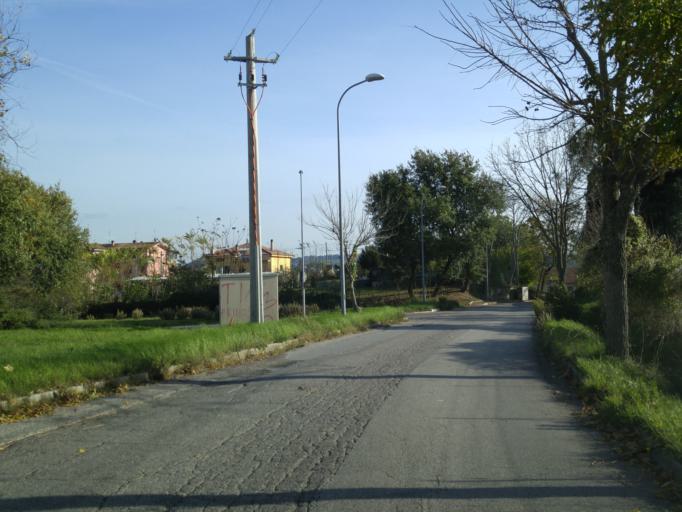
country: IT
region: The Marches
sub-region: Provincia di Pesaro e Urbino
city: Calcinelli
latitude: 43.7508
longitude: 12.9117
